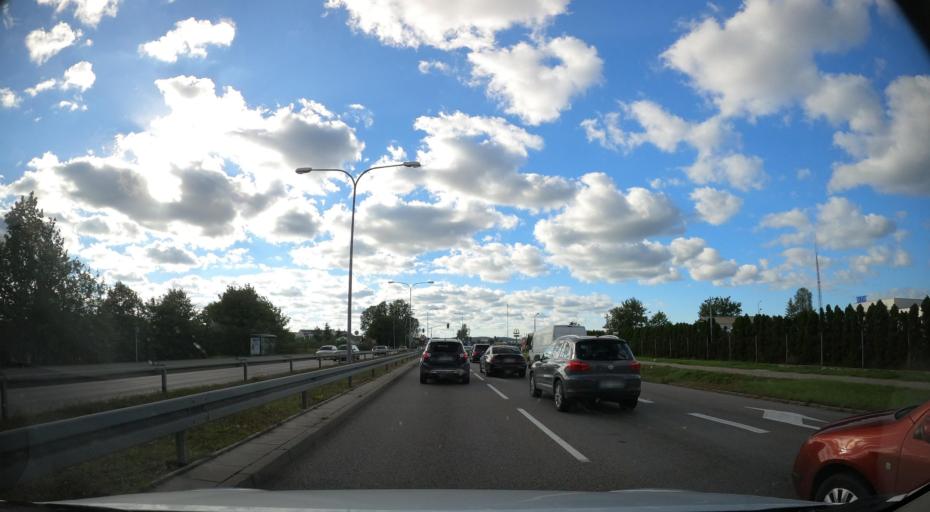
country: PL
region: Pomeranian Voivodeship
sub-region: Powiat wejherowski
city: Bolszewo
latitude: 54.6093
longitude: 18.2012
